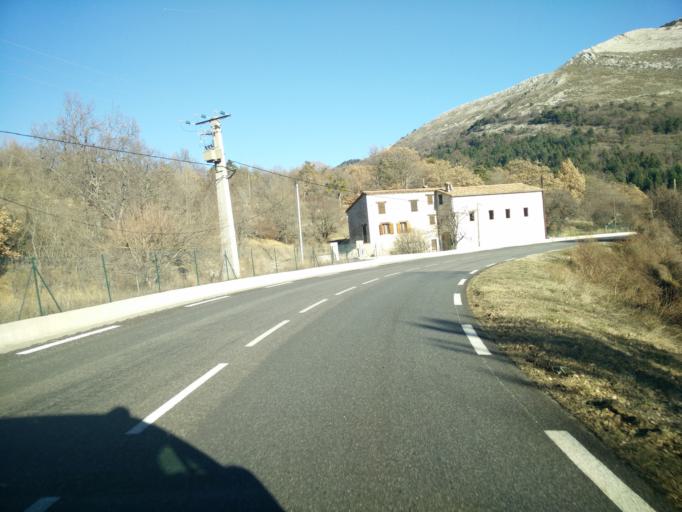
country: FR
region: Provence-Alpes-Cote d'Azur
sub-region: Departement des Alpes-Maritimes
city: Saint-Vallier-de-Thiey
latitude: 43.7186
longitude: 6.8544
